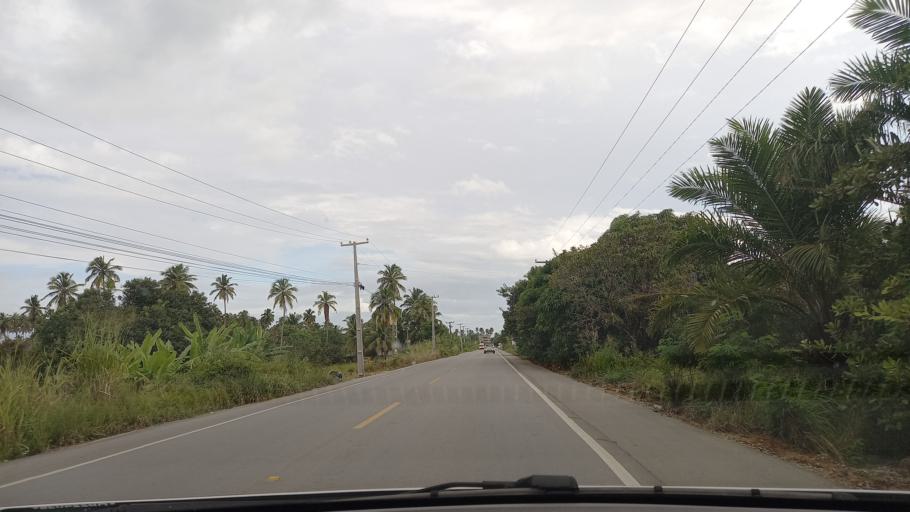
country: BR
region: Alagoas
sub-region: Maragogi
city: Maragogi
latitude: -8.9714
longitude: -35.1831
